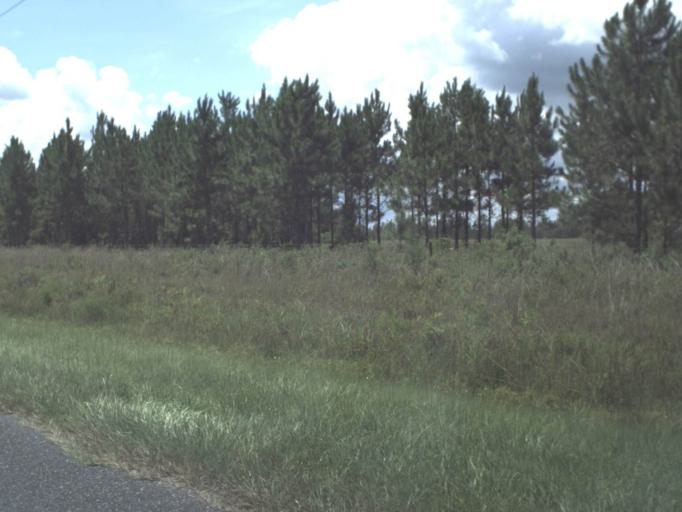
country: US
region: Florida
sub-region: Levy County
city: Bronson
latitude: 29.4652
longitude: -82.6673
